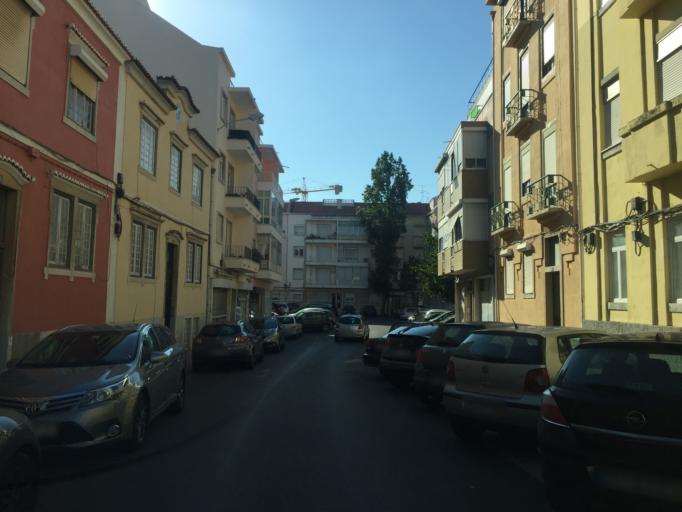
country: PT
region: Lisbon
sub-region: Odivelas
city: Pontinha
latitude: 38.7450
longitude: -9.1785
